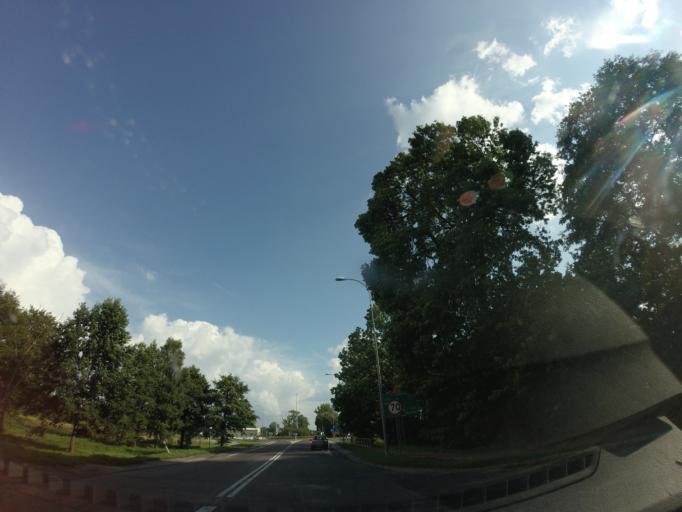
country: PL
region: Masovian Voivodeship
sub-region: Siedlce
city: Siedlce
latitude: 52.1340
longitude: 22.2909
